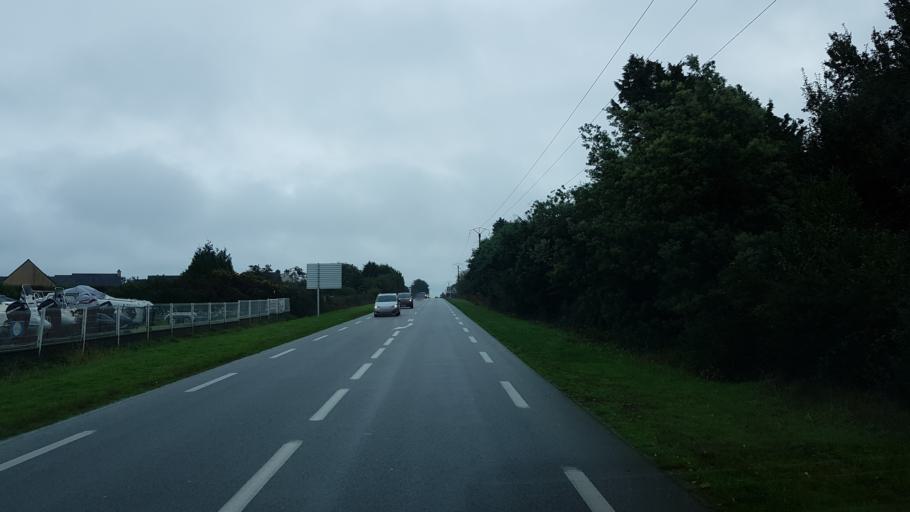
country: FR
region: Brittany
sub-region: Departement du Morbihan
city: Sarzeau
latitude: 47.5256
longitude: -2.7916
